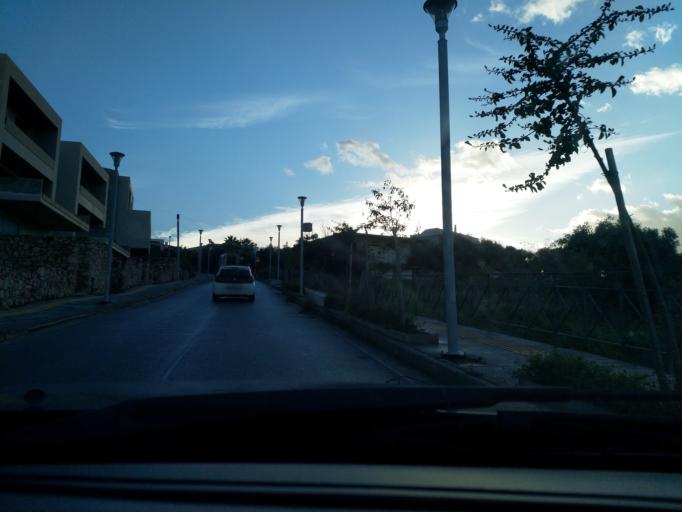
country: GR
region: Crete
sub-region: Nomos Chanias
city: Chania
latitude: 35.5121
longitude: 24.0465
